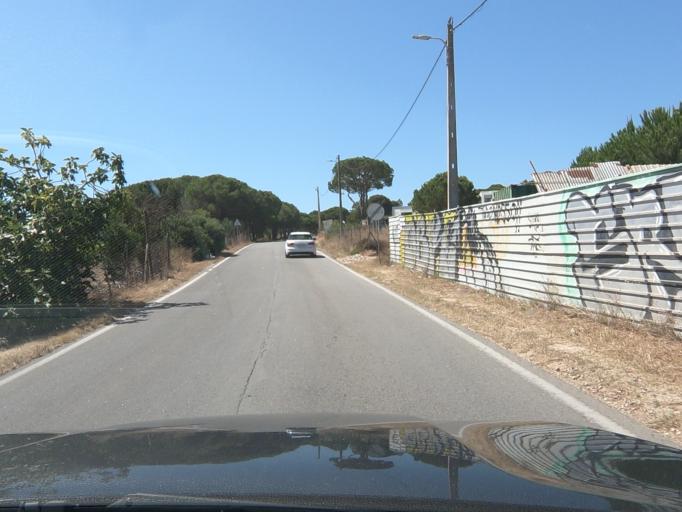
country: PT
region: Faro
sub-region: Loule
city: Vilamoura
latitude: 37.0973
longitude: -8.0975
